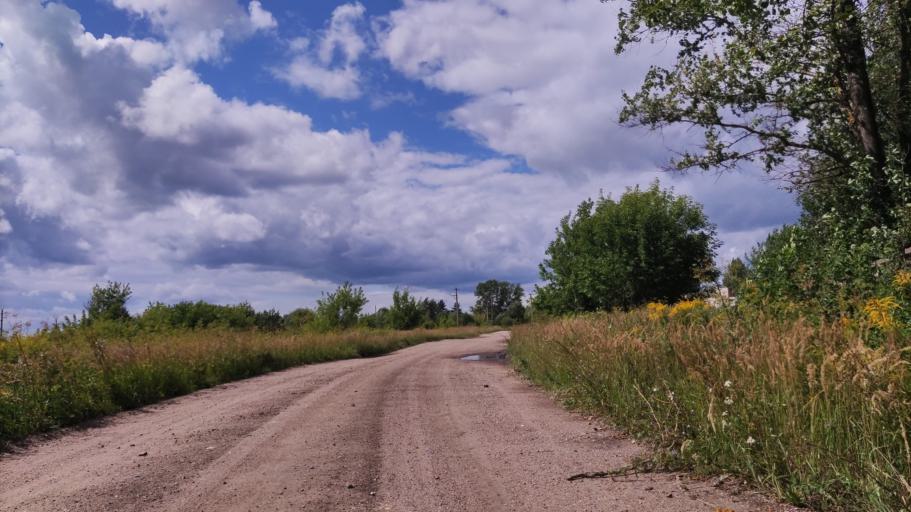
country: RU
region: Tverskaya
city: Rzhev
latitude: 56.2393
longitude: 34.3092
